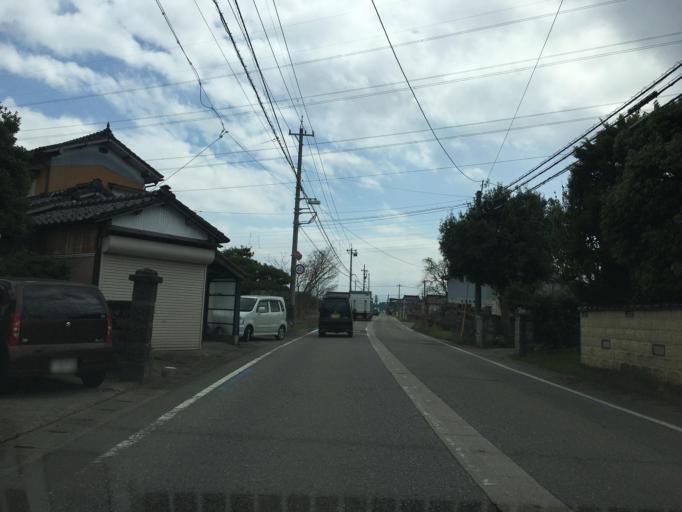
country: JP
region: Toyama
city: Kuragaki-kosugi
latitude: 36.6958
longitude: 137.1157
